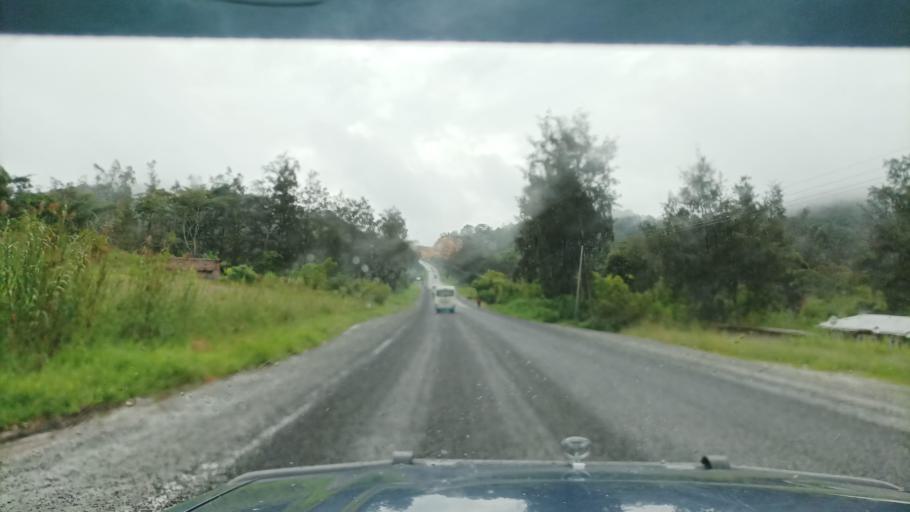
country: PG
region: Western Highlands
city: Rauna
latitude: -5.8319
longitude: 144.3650
